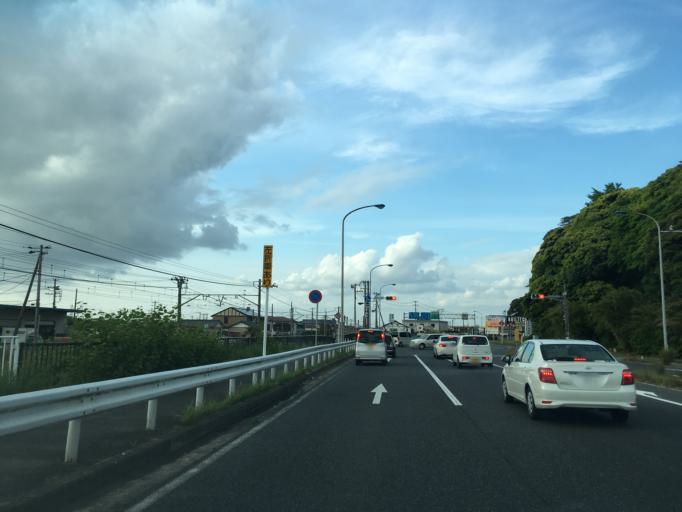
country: JP
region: Chiba
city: Kisarazu
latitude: 35.3627
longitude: 139.9223
